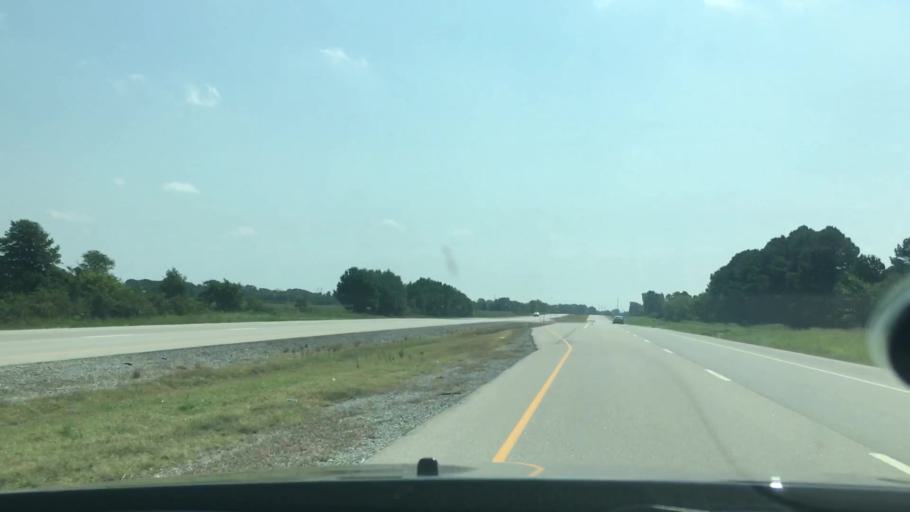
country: US
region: Oklahoma
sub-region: Atoka County
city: Atoka
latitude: 34.3412
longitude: -96.0680
